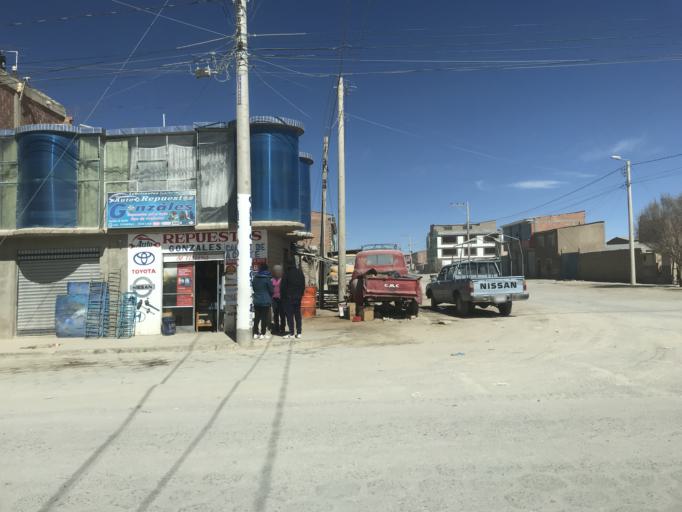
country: BO
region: Potosi
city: Uyuni
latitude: -20.4561
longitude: -66.8285
